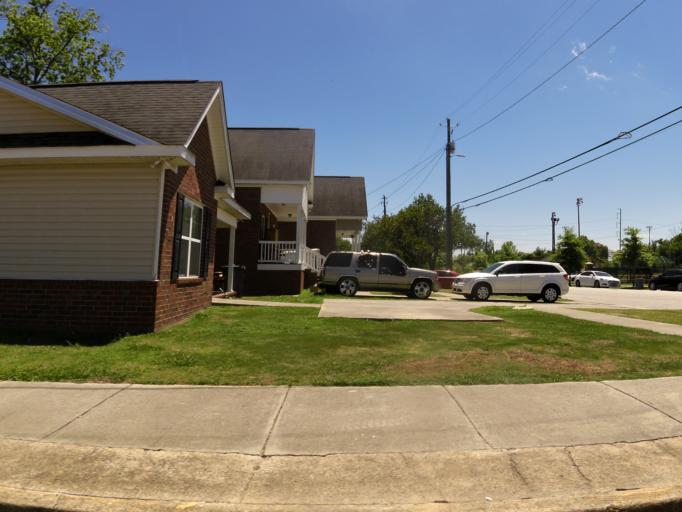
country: US
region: Georgia
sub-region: Richmond County
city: Augusta
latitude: 33.4675
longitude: -81.9719
